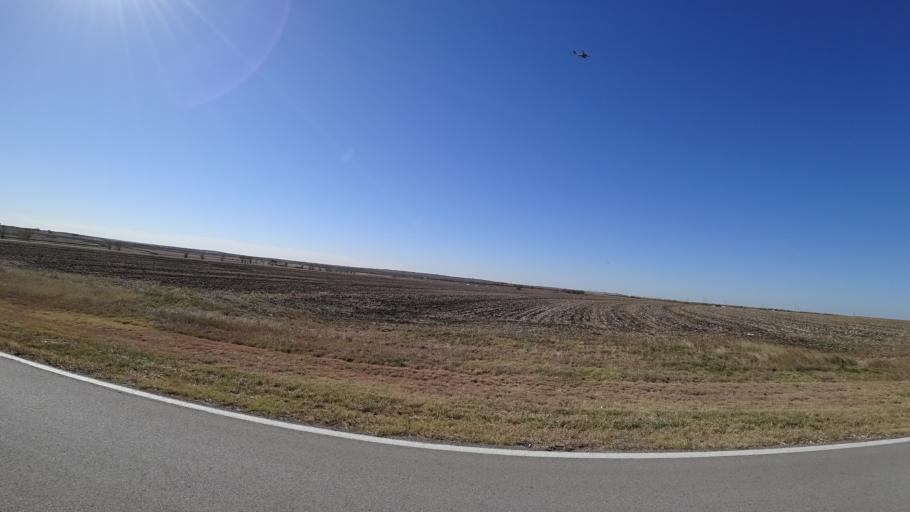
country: US
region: Texas
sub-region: Travis County
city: Garfield
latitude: 30.1004
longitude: -97.6383
